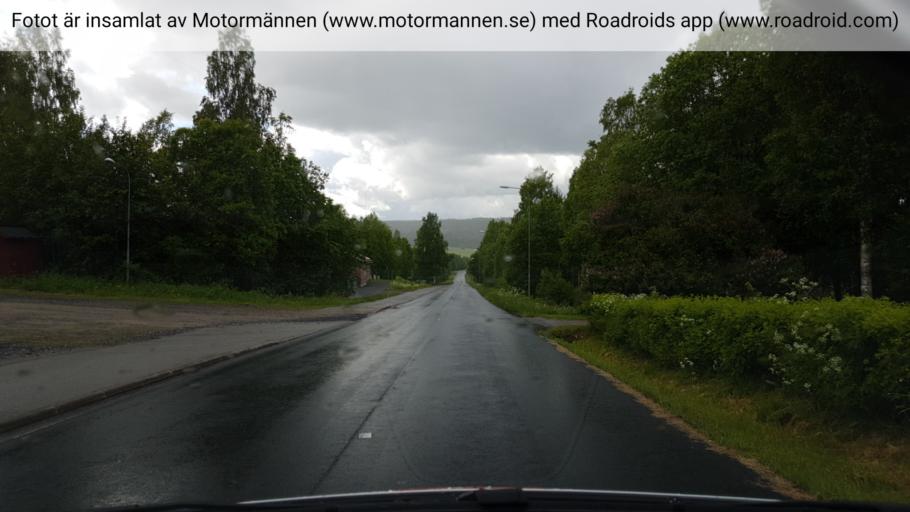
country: SE
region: Vaesterbotten
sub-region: Vannas Kommun
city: Vannasby
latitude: 63.8515
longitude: 19.9261
